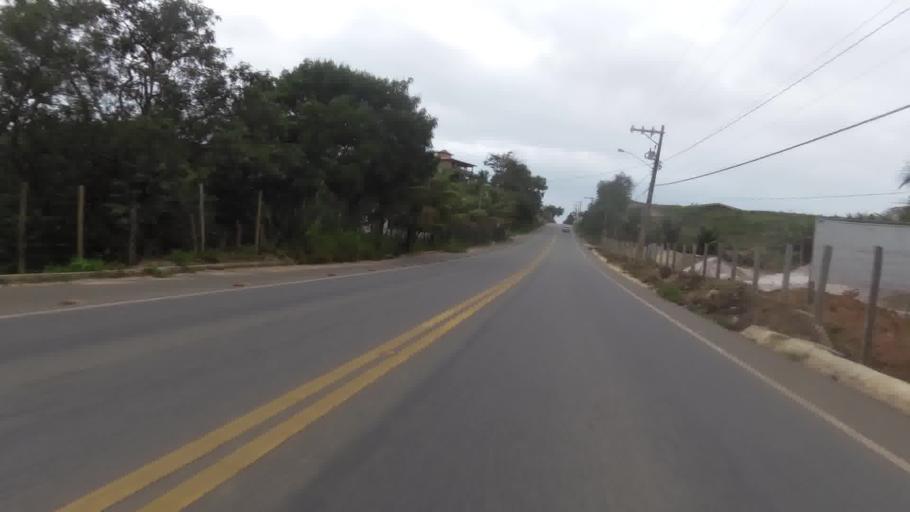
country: BR
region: Espirito Santo
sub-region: Piuma
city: Piuma
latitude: -20.8159
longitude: -40.7340
